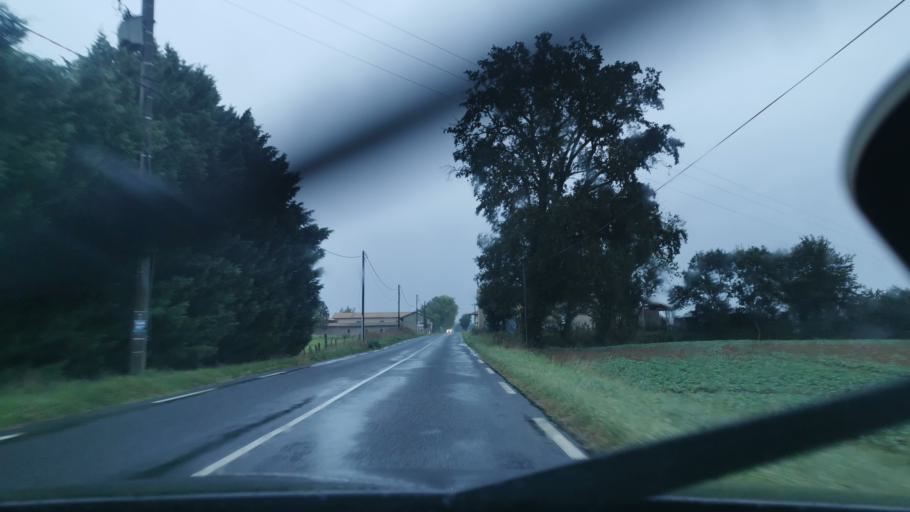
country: FR
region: Rhone-Alpes
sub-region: Departement de l'Ain
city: Amberieux-en-Dombes
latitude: 46.0243
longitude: 4.8982
